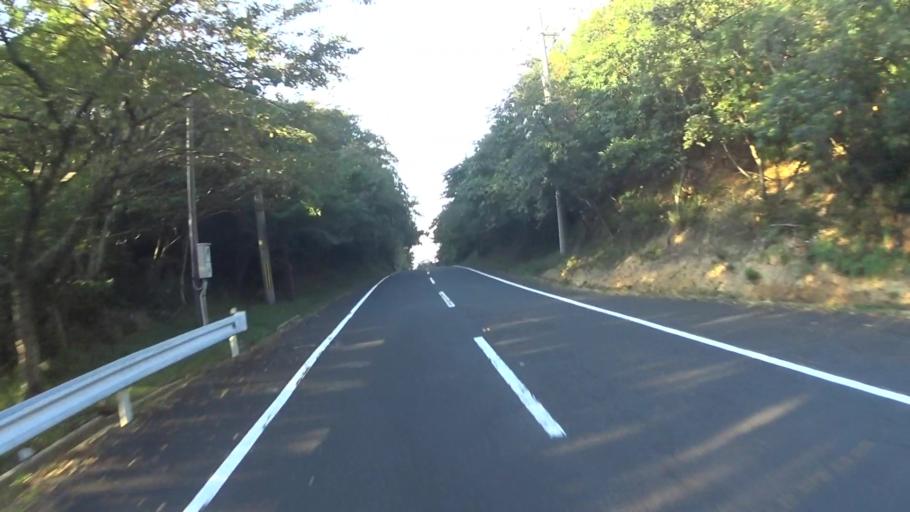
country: JP
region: Hyogo
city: Toyooka
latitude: 35.6886
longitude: 134.9873
